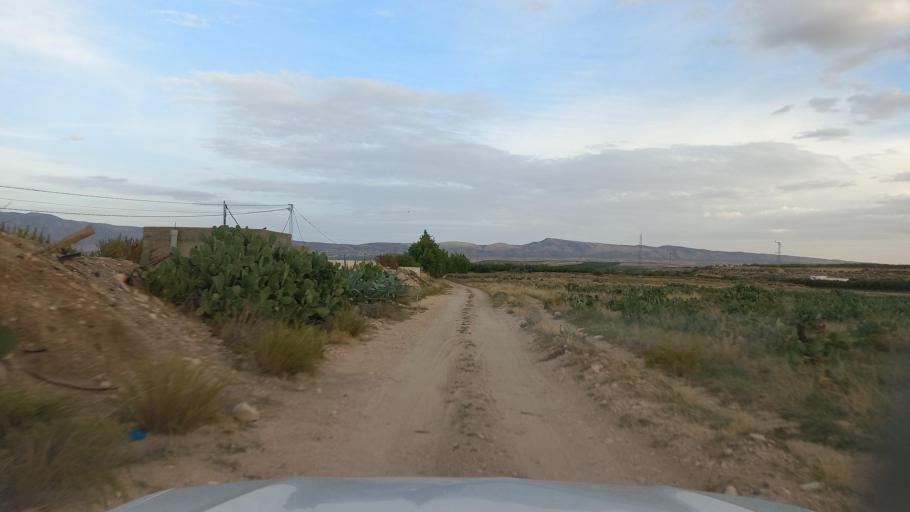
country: TN
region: Al Qasrayn
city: Sbiba
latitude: 35.4253
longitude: 9.0962
